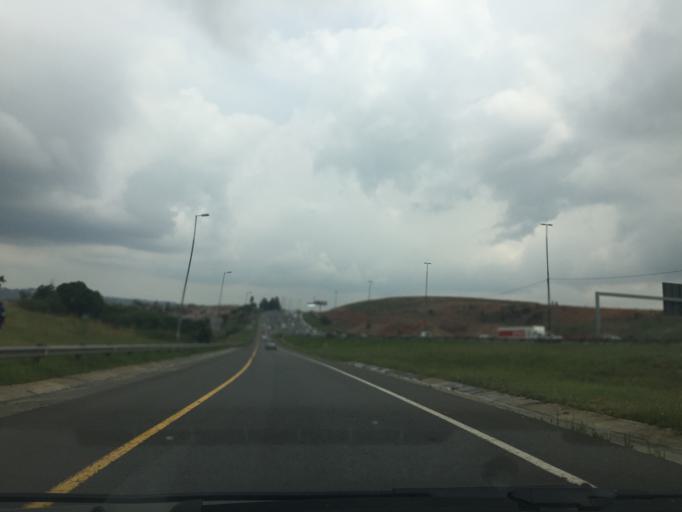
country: ZA
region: Gauteng
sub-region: City of Johannesburg Metropolitan Municipality
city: Modderfontein
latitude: -26.1029
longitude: 28.1230
